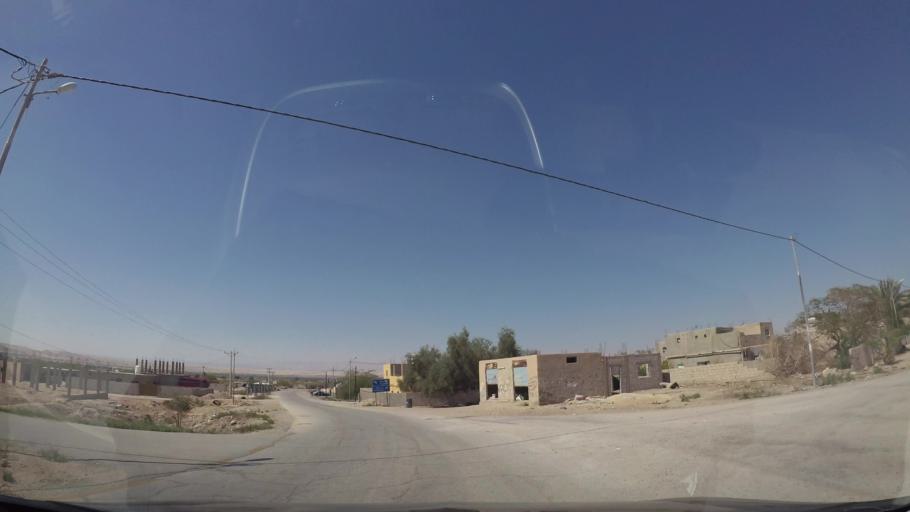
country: JO
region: Karak
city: Safi
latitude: 30.9162
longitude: 35.4602
